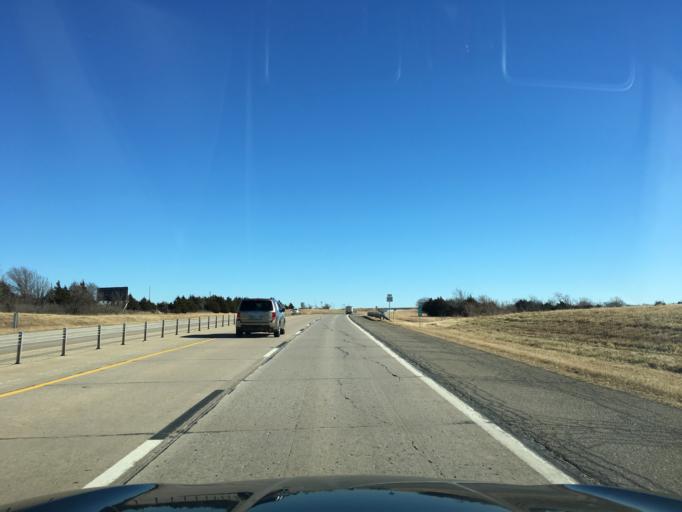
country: US
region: Oklahoma
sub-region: Pawnee County
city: Pawnee
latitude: 36.2393
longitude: -96.9350
